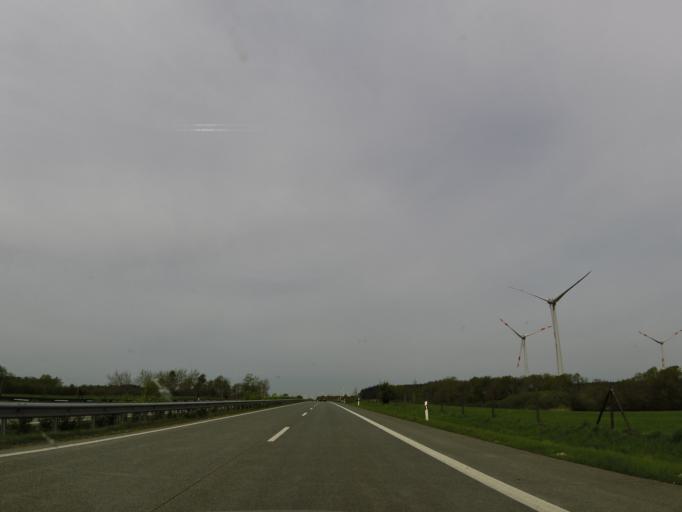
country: DE
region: Schleswig-Holstein
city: Nienbuttel
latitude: 54.0383
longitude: 9.4242
